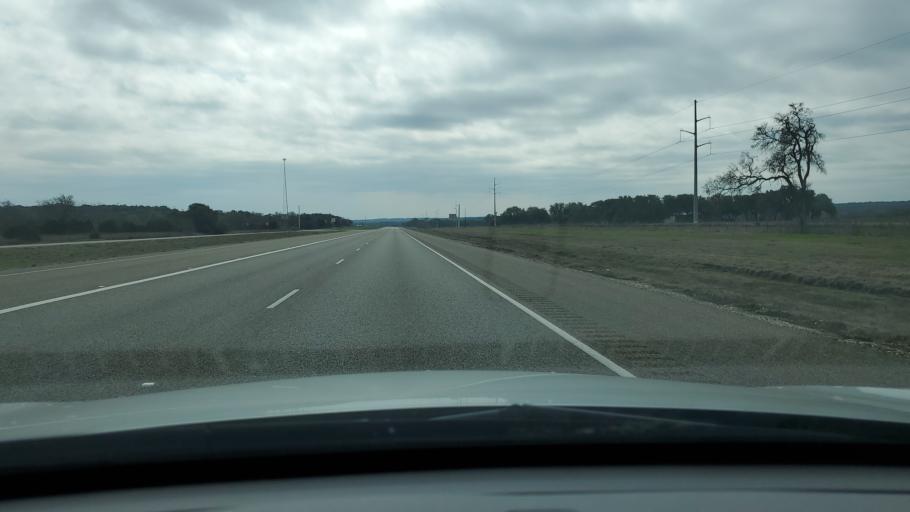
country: US
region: Texas
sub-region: Williamson County
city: Florence
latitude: 30.7815
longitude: -97.7622
